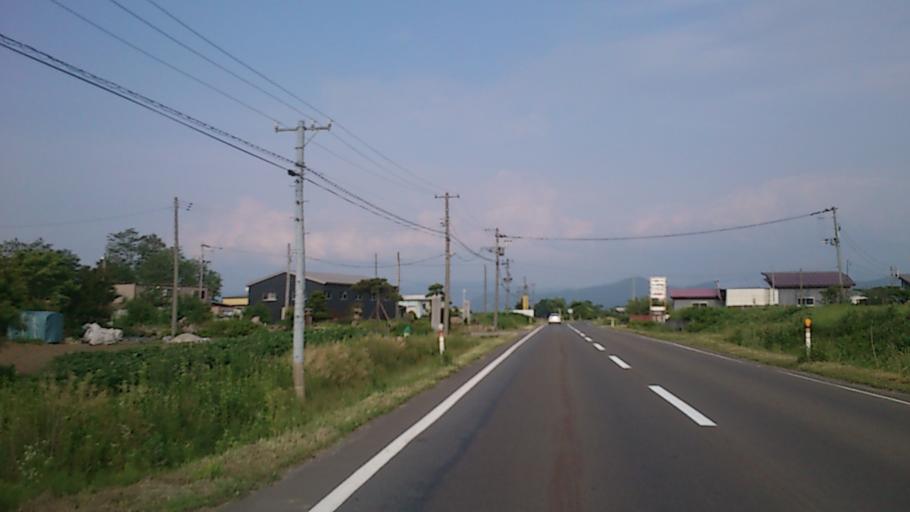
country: JP
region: Aomori
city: Hirosaki
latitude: 40.5584
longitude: 140.5014
